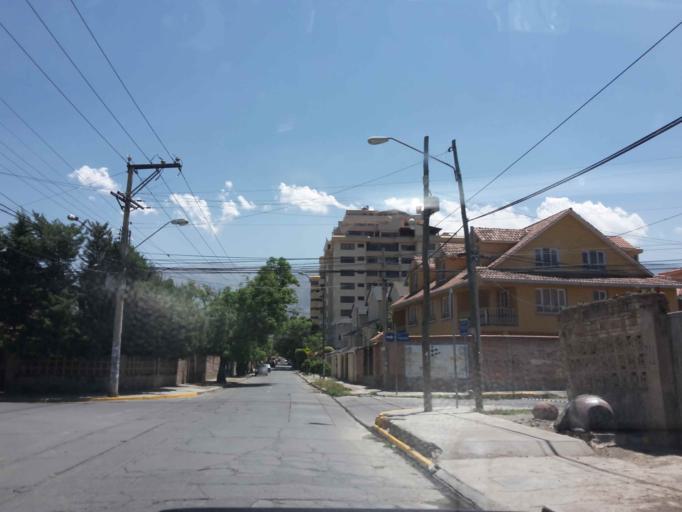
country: BO
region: Cochabamba
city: Cochabamba
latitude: -17.3759
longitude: -66.1851
